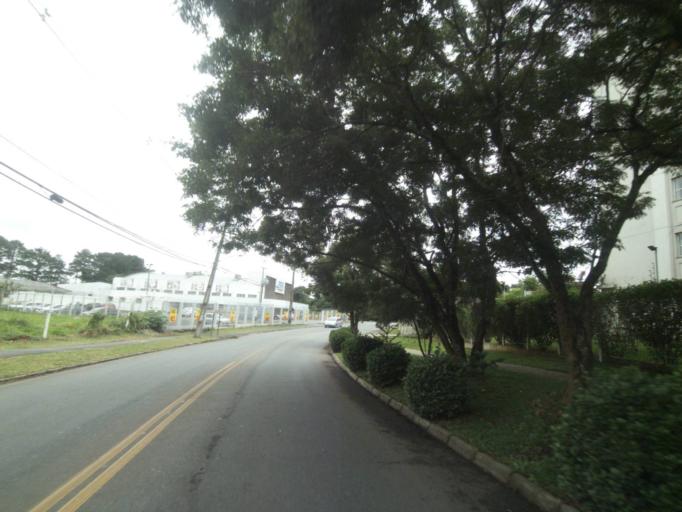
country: BR
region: Parana
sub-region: Curitiba
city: Curitiba
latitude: -25.4619
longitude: -49.3300
